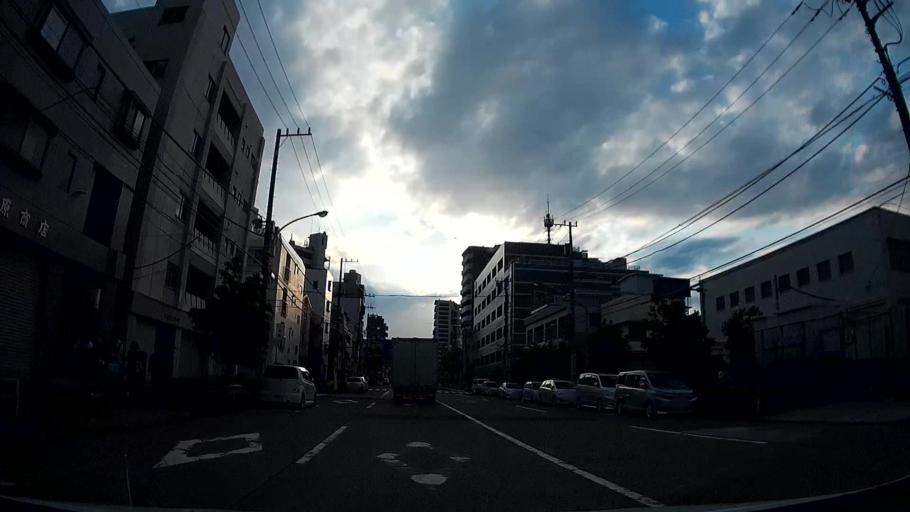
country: JP
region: Saitama
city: Kawaguchi
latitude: 35.7591
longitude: 139.7395
